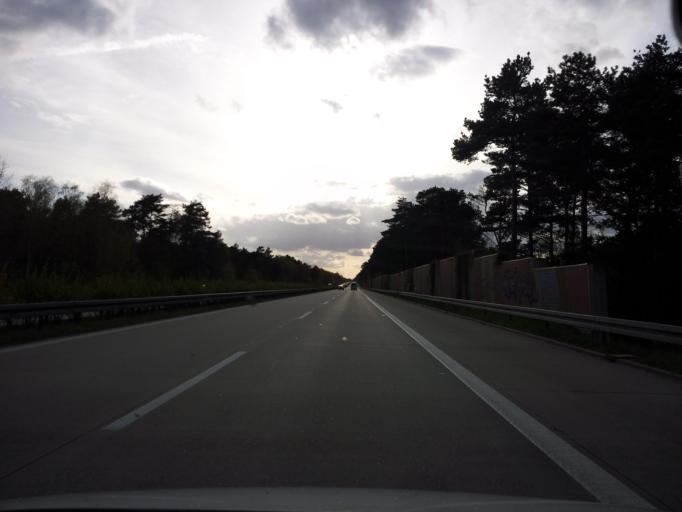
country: DE
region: Brandenburg
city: Cottbus
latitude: 51.7169
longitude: 14.3745
